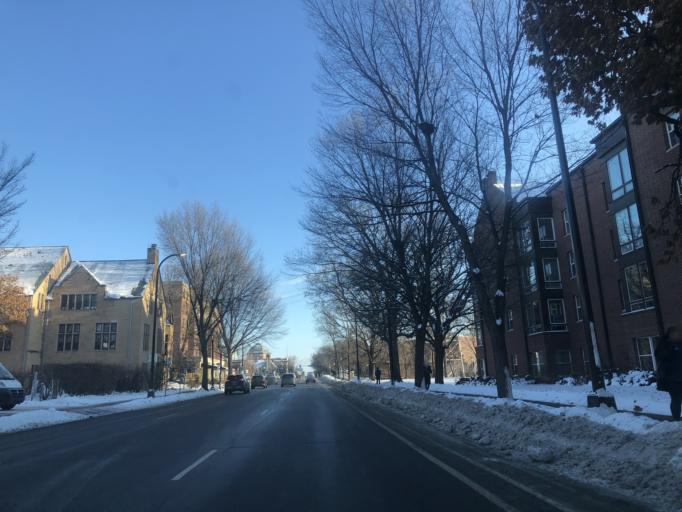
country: US
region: Minnesota
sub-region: Hennepin County
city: Minneapolis
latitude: 44.9804
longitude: -93.2389
